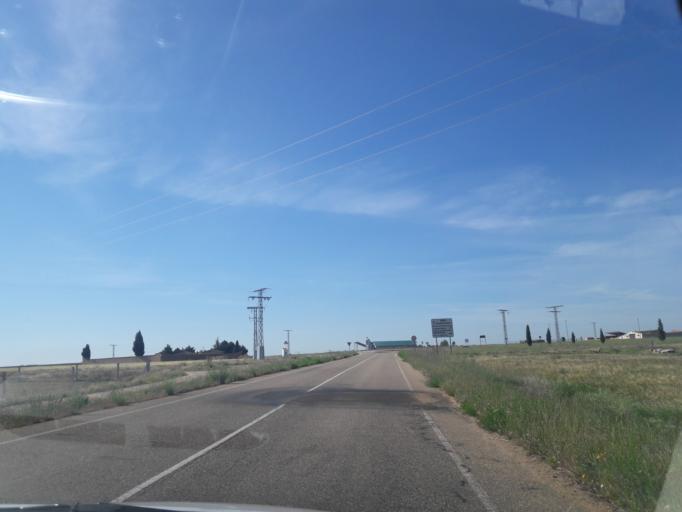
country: ES
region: Castille and Leon
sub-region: Provincia de Salamanca
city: Espino de la Orbada
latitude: 41.0813
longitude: -5.3946
